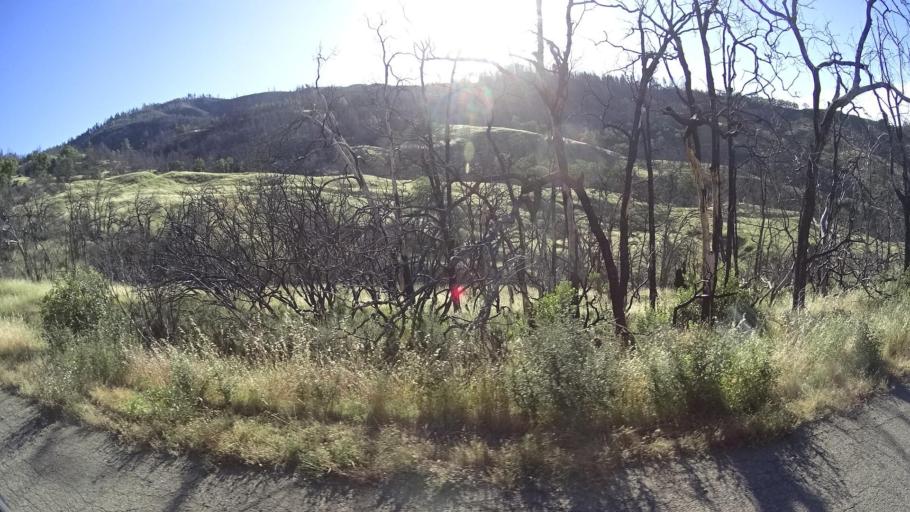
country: US
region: California
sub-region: Lake County
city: Upper Lake
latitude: 39.2689
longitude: -122.9261
